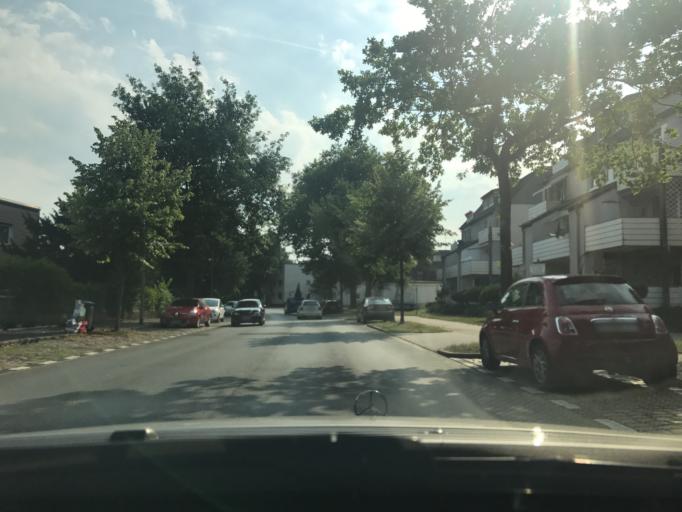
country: DE
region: North Rhine-Westphalia
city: Meiderich
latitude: 51.4918
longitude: 6.7973
